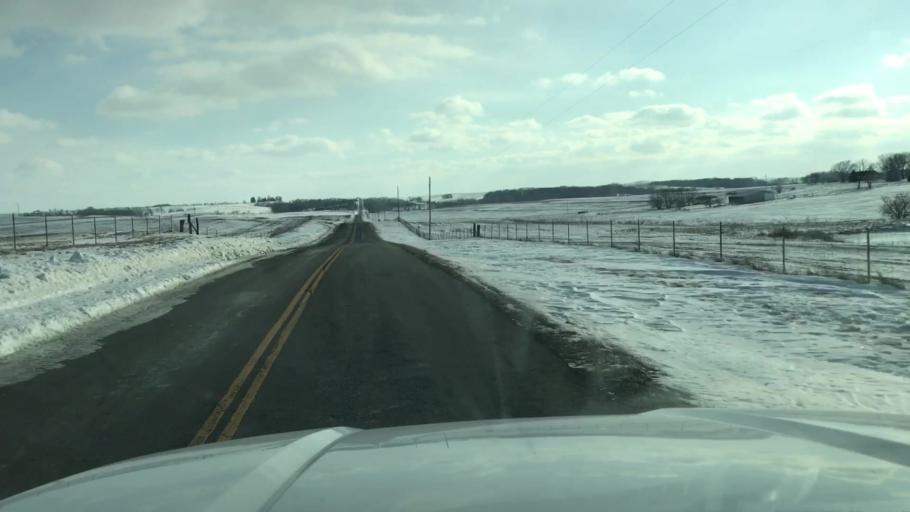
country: US
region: Missouri
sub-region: Nodaway County
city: Maryville
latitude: 40.1849
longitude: -95.0123
